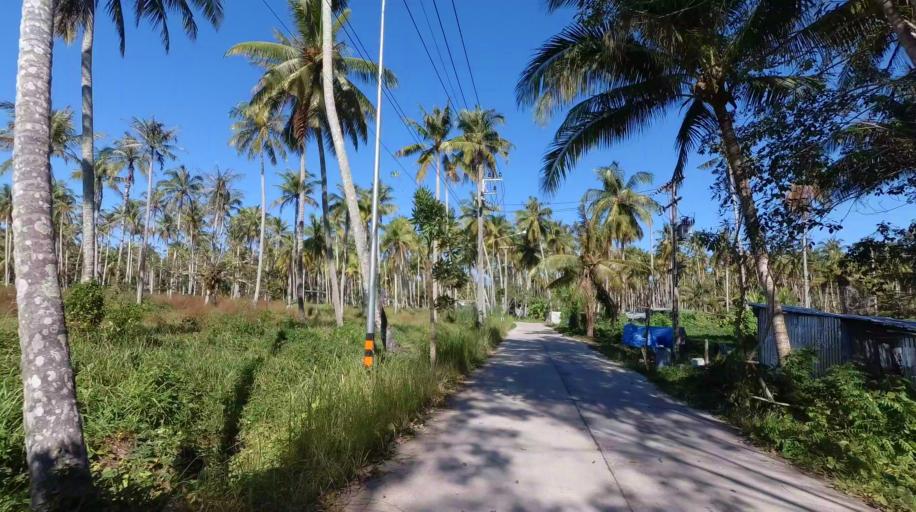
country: TH
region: Trat
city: Ko Kut
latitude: 11.6209
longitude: 102.5497
